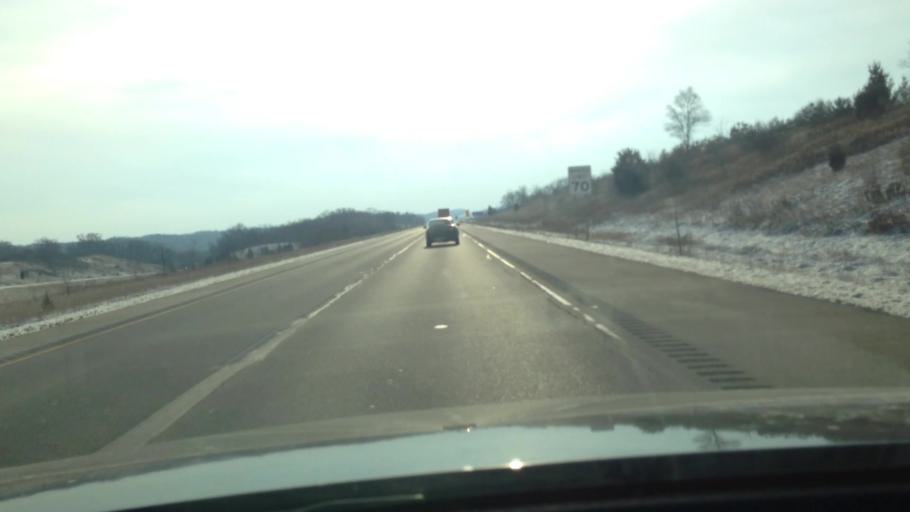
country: US
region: Wisconsin
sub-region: Walworth County
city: East Troy
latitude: 42.7407
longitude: -88.4538
